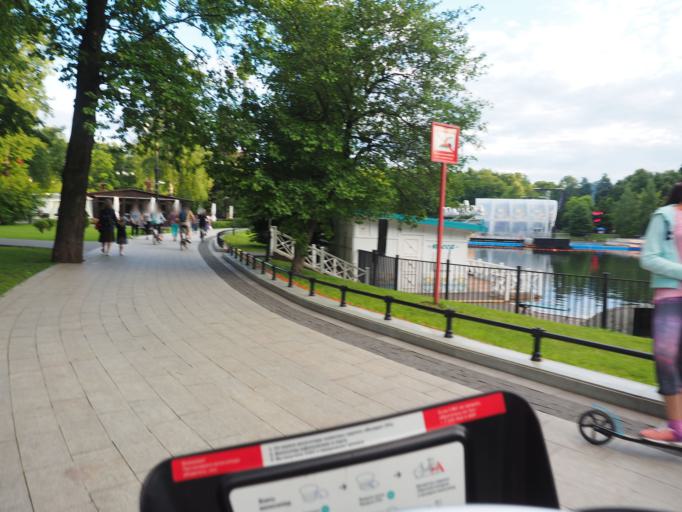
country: RU
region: Moscow
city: Ostankinskiy
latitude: 55.8298
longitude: 37.6173
